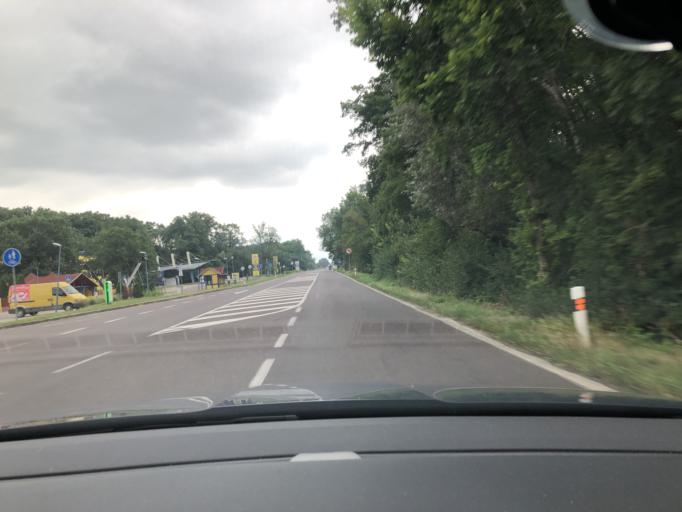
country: AT
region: Lower Austria
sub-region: Politischer Bezirk Mistelbach
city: Laa an der Thaya
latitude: 48.7313
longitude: 16.3832
